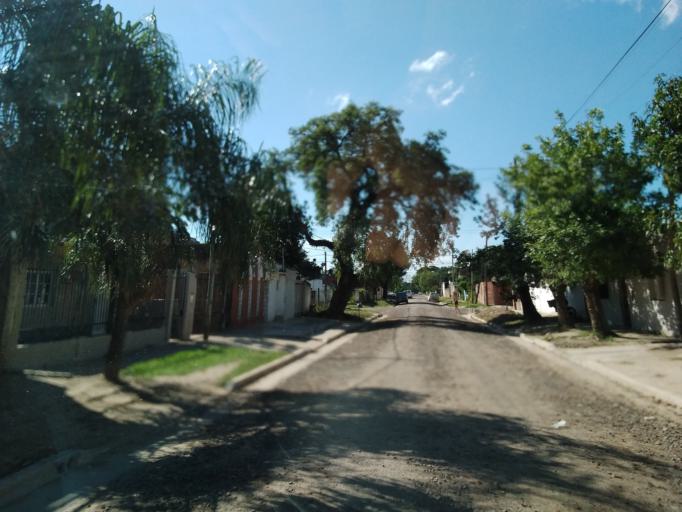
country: AR
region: Corrientes
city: Corrientes
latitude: -27.4842
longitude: -58.8106
